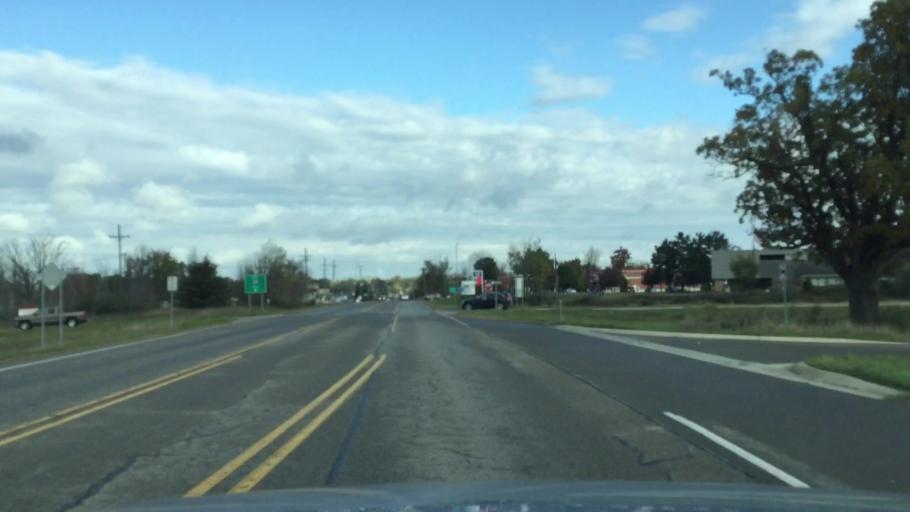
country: US
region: Michigan
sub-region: Lapeer County
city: Lapeer
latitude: 43.0327
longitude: -83.3615
